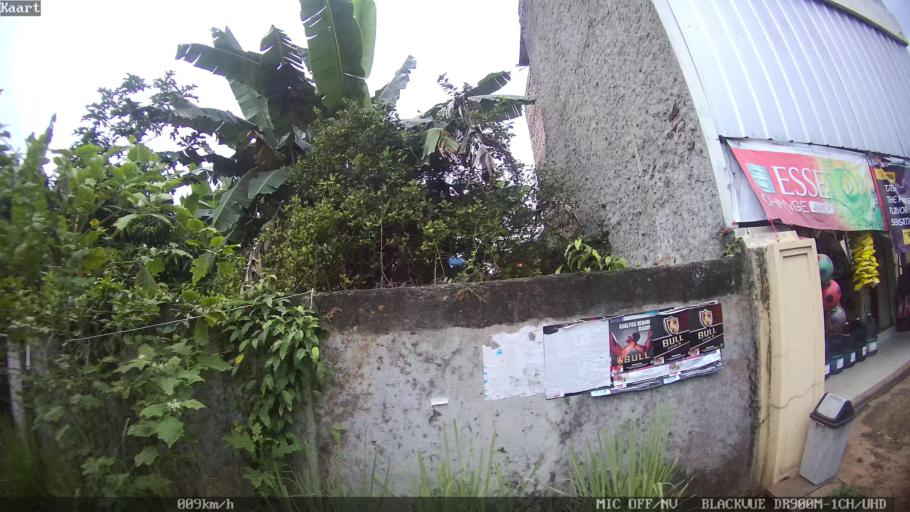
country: ID
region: Lampung
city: Kedaton
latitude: -5.3834
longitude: 105.2523
